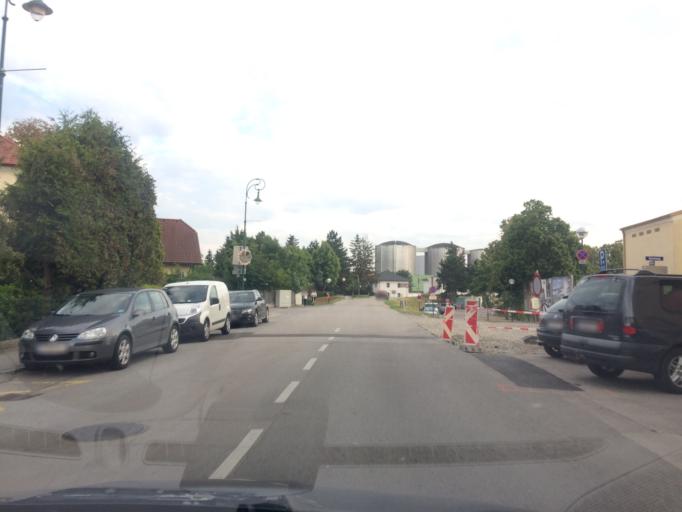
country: AT
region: Lower Austria
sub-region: Politischer Bezirk Tulln
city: Tulln
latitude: 48.3292
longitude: 16.0440
